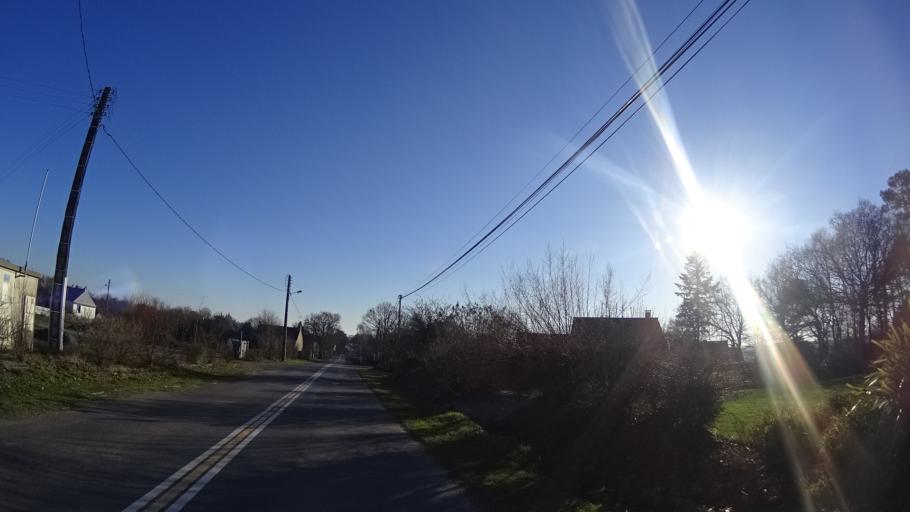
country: FR
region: Brittany
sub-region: Departement du Morbihan
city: Allaire
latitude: 47.6437
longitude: -2.1669
